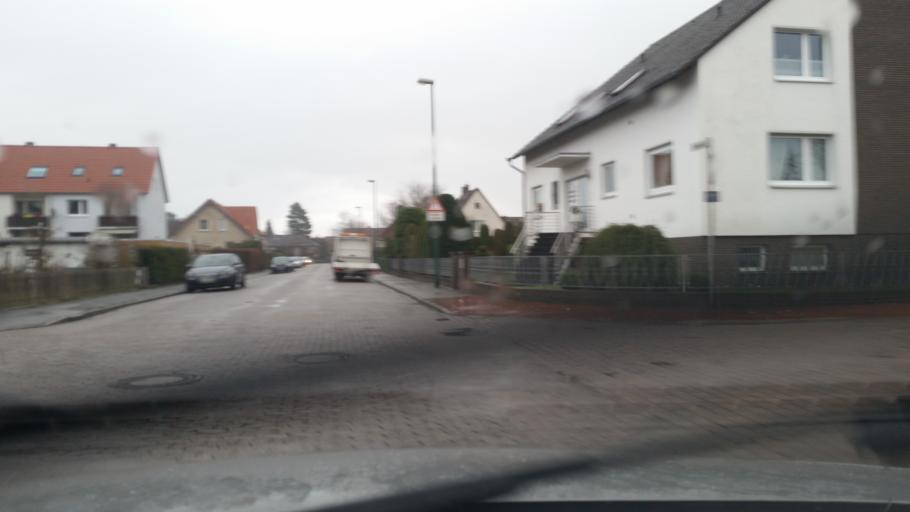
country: DE
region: Lower Saxony
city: Langenhagen
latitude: 52.4629
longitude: 9.7425
